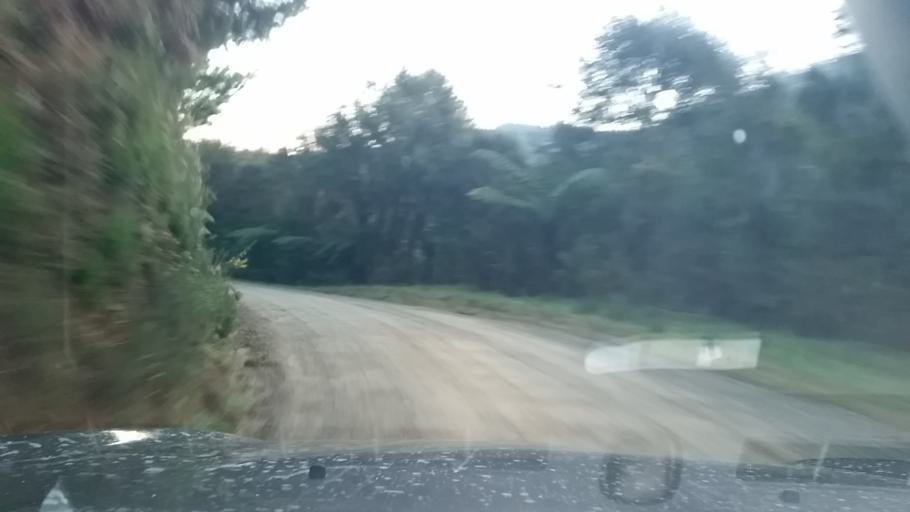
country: NZ
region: Marlborough
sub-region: Marlborough District
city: Picton
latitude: -41.1376
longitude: 174.1419
